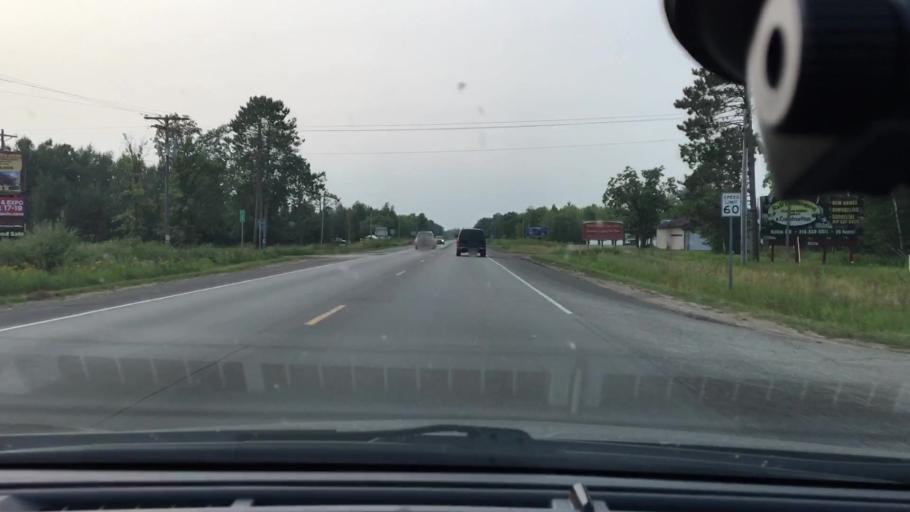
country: US
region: Minnesota
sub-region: Mille Lacs County
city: Vineland
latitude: 46.3008
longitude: -93.8278
